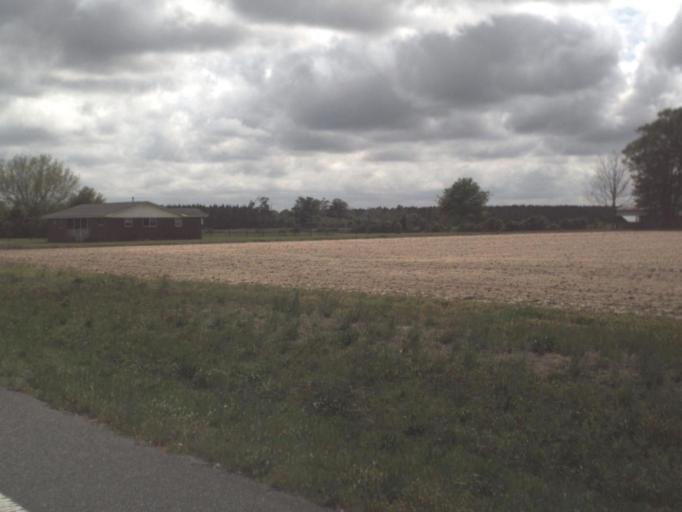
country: US
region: Florida
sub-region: Santa Rosa County
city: Point Baker
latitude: 30.7714
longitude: -87.0929
